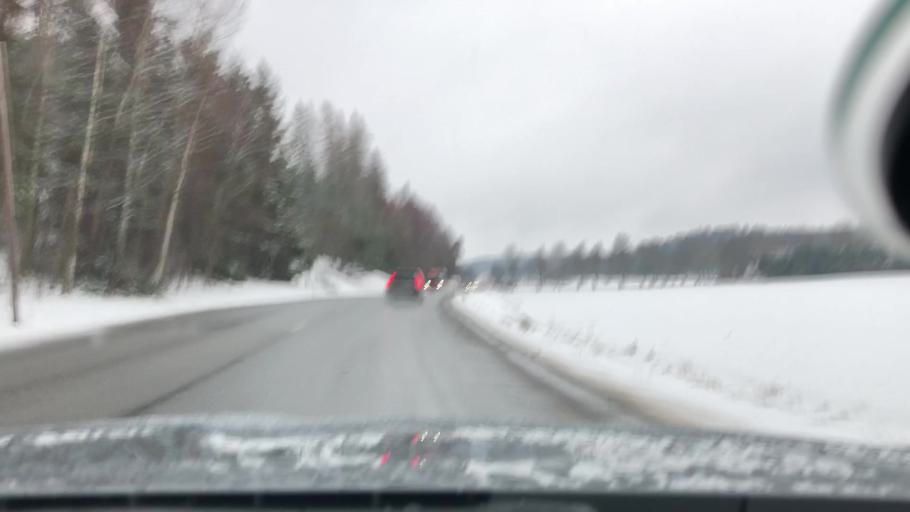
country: SE
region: Stockholm
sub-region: Sodertalje Kommun
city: Pershagen
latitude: 59.0577
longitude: 17.6132
